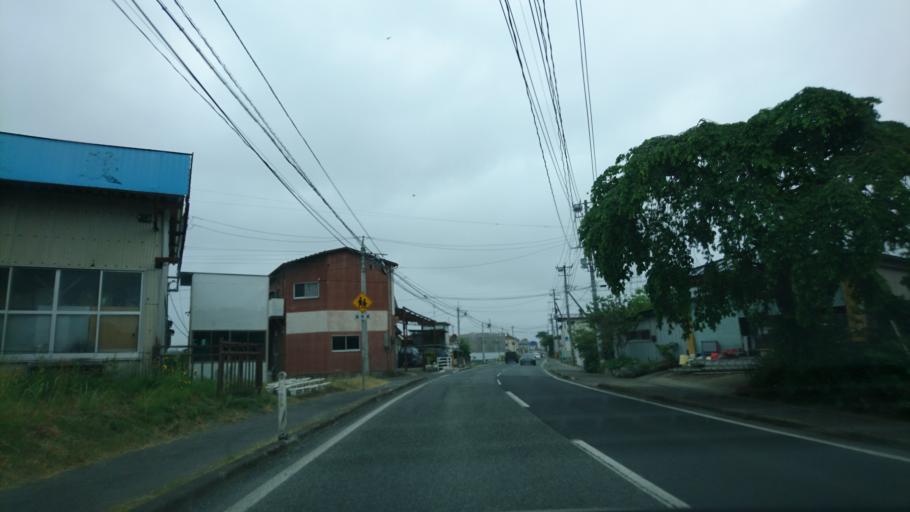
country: JP
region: Iwate
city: Ichinoseki
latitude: 38.9290
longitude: 141.1551
